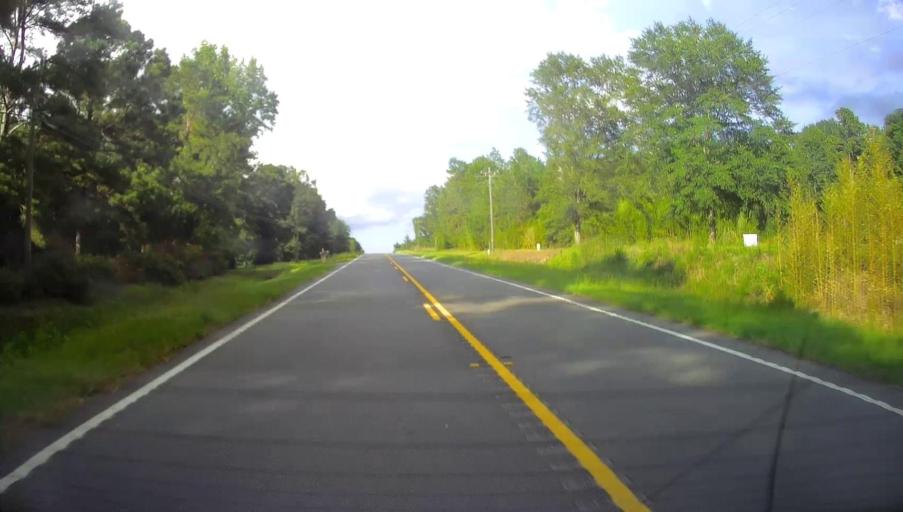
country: US
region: Georgia
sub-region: Crawford County
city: Knoxville
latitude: 32.7347
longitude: -83.9841
